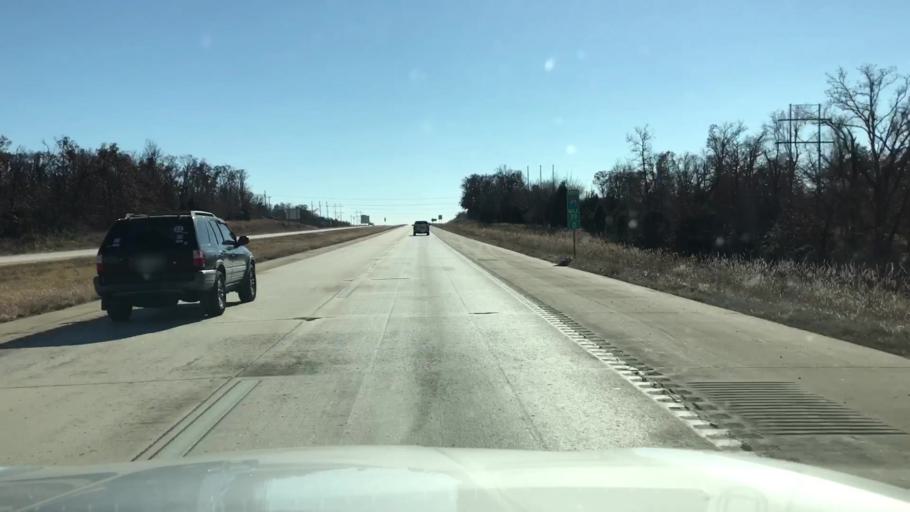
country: US
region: Missouri
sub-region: Jasper County
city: Duenweg
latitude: 37.0467
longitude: -94.4277
